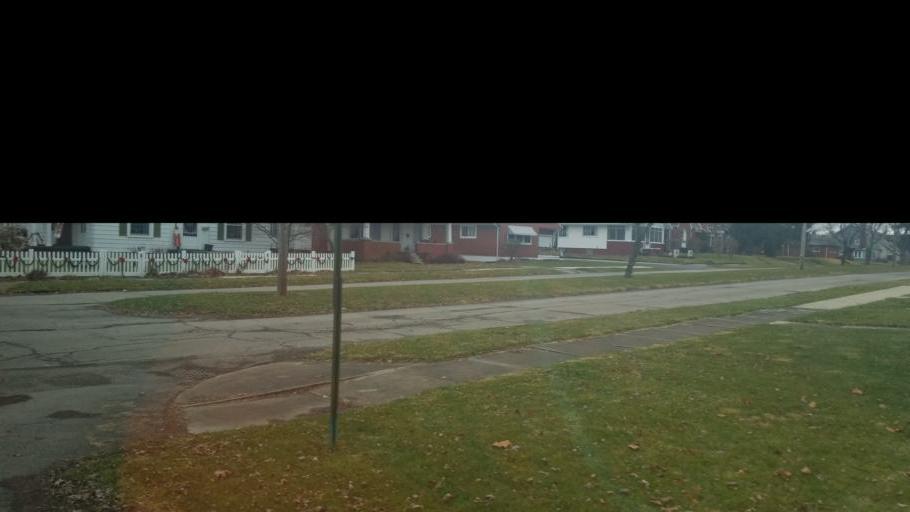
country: US
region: Ohio
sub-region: Crawford County
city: Crestline
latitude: 40.7885
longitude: -82.7461
